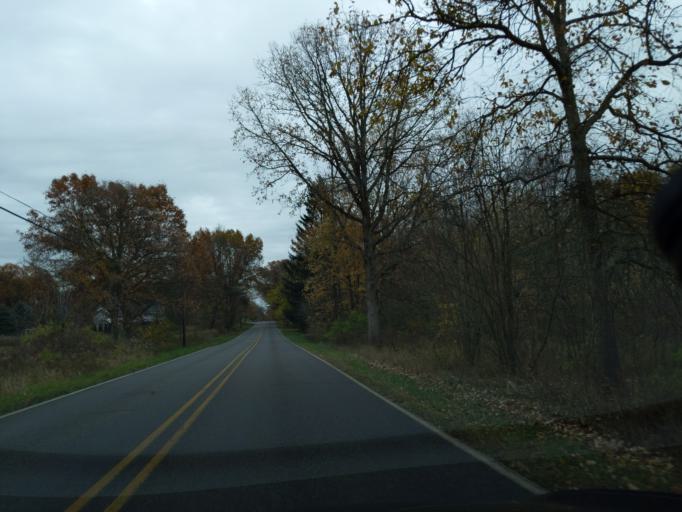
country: US
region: Michigan
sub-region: Jackson County
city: Spring Arbor
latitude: 42.2767
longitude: -84.5744
